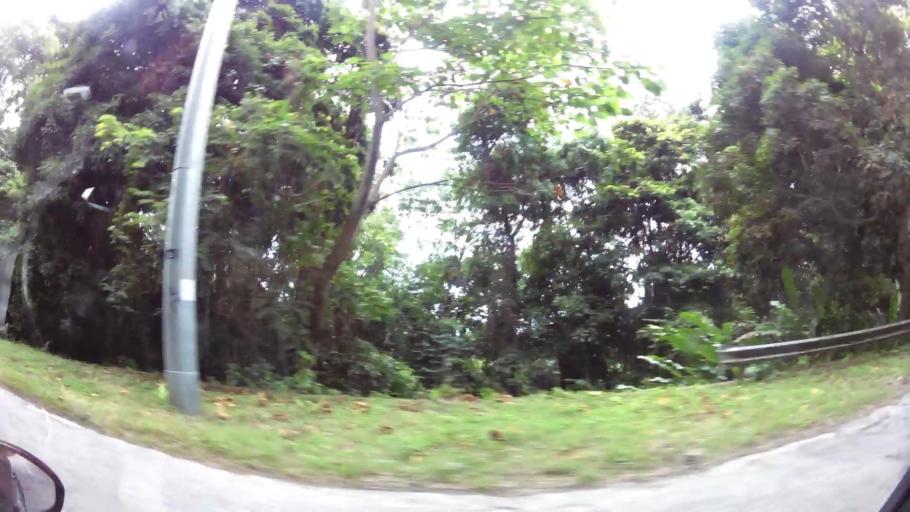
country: TT
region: Diego Martin
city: Petit Valley
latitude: 10.7469
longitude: -61.4855
